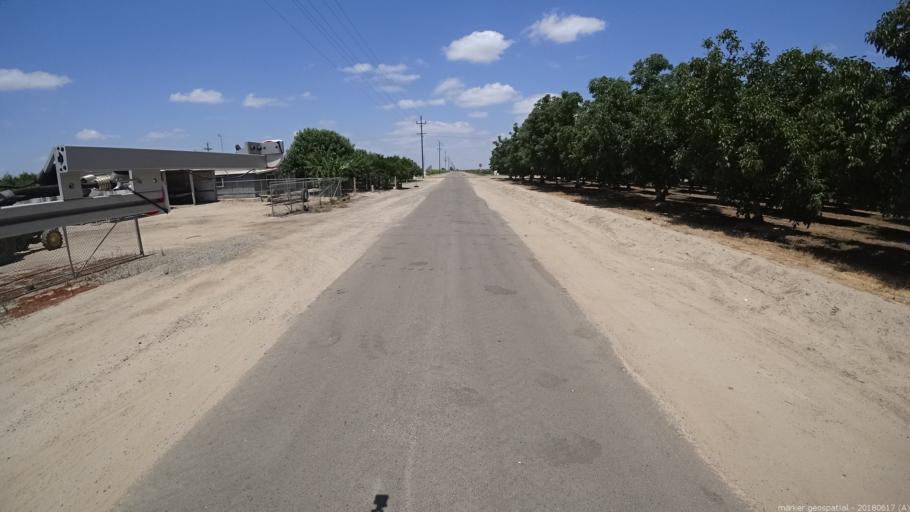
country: US
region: California
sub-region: Fresno County
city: Biola
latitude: 36.8214
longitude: -120.1149
